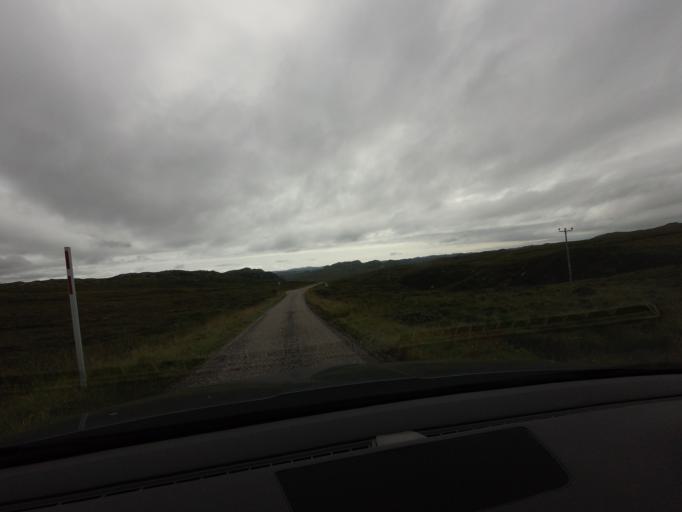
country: GB
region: Scotland
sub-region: Highland
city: Ullapool
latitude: 58.4471
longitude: -4.9441
